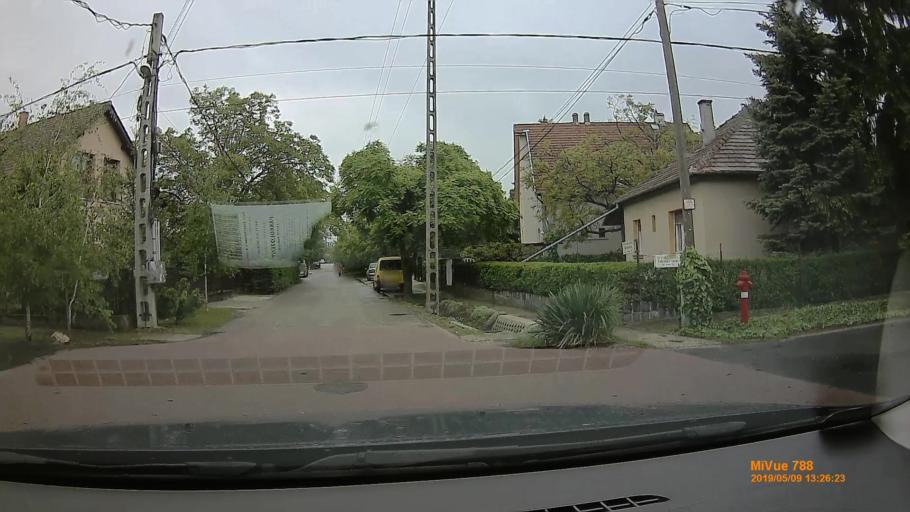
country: HU
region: Budapest
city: Budapest XVI. keruelet
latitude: 47.5366
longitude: 19.1892
